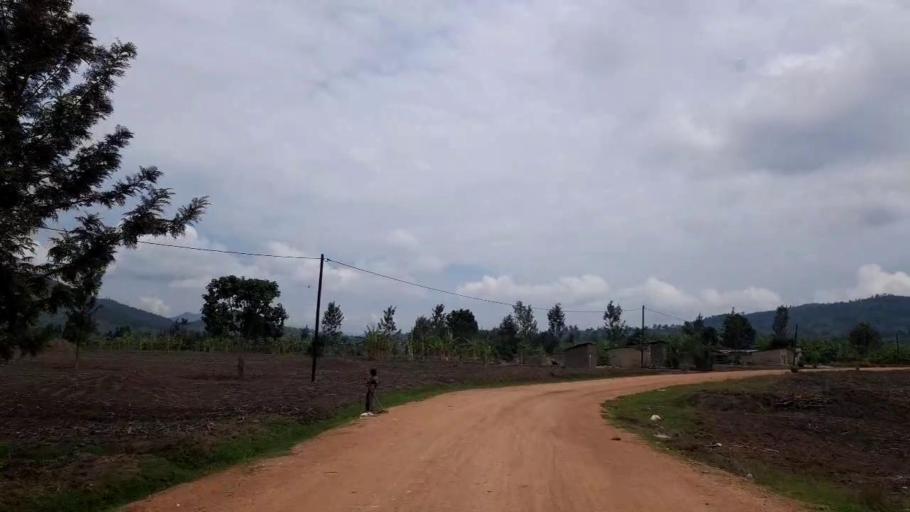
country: RW
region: Northern Province
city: Byumba
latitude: -1.4995
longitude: 30.2075
